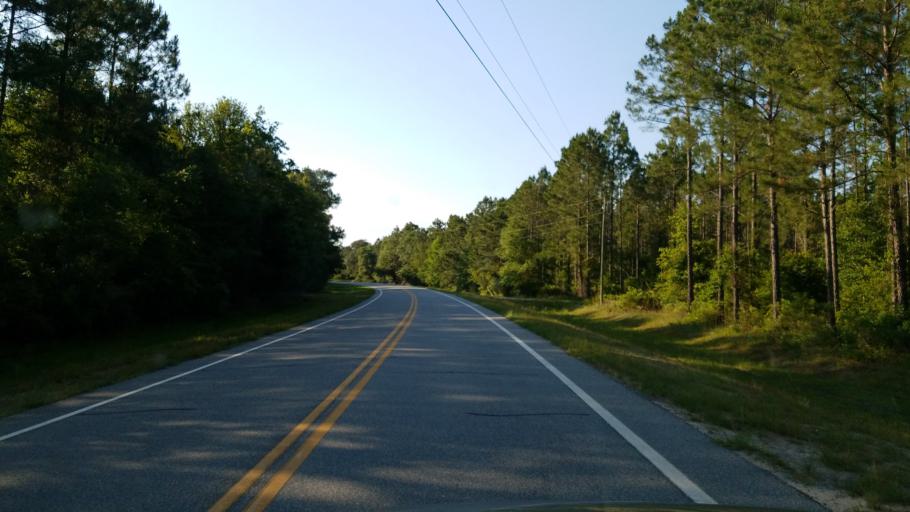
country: US
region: Georgia
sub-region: Lanier County
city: Lakeland
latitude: 30.8859
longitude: -83.0533
